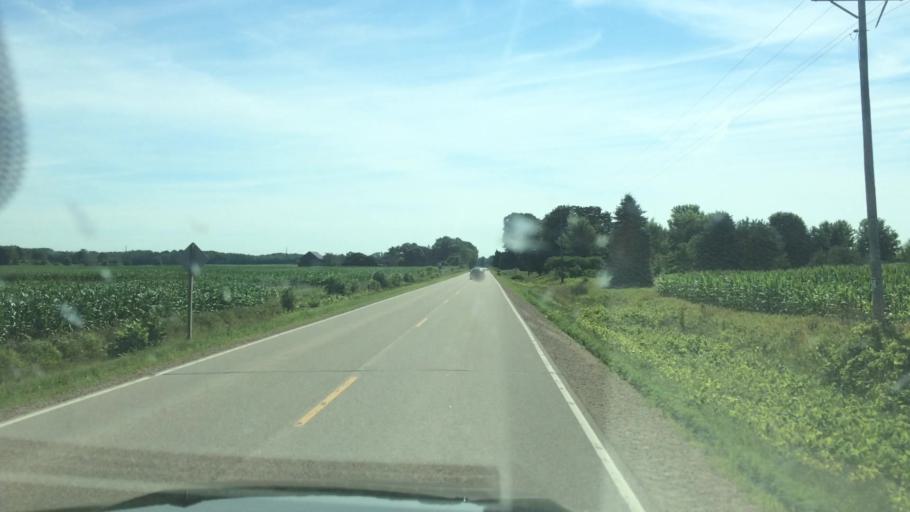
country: US
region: Wisconsin
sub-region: Oconto County
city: Gillett
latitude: 44.7875
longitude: -88.3283
